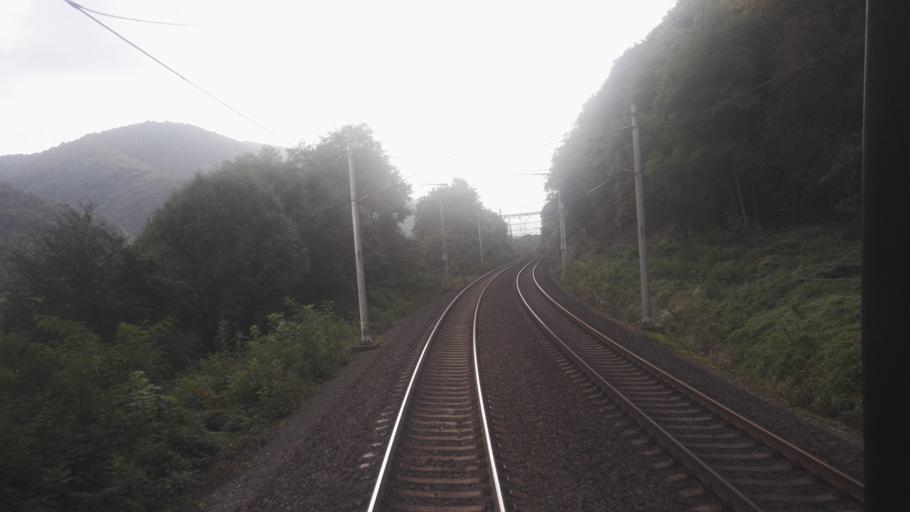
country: CZ
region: Ustecky
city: Povrly
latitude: 50.6922
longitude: 14.1956
